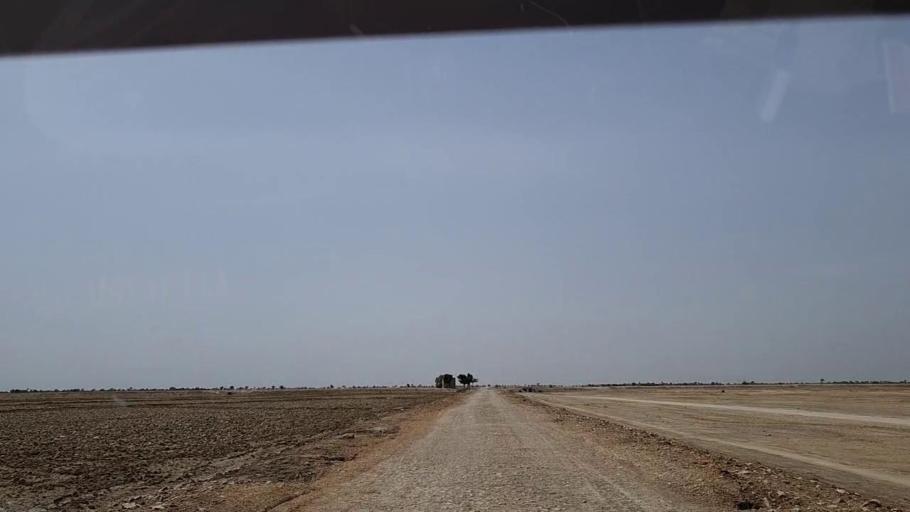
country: PK
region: Sindh
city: Johi
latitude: 26.7293
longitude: 67.6392
